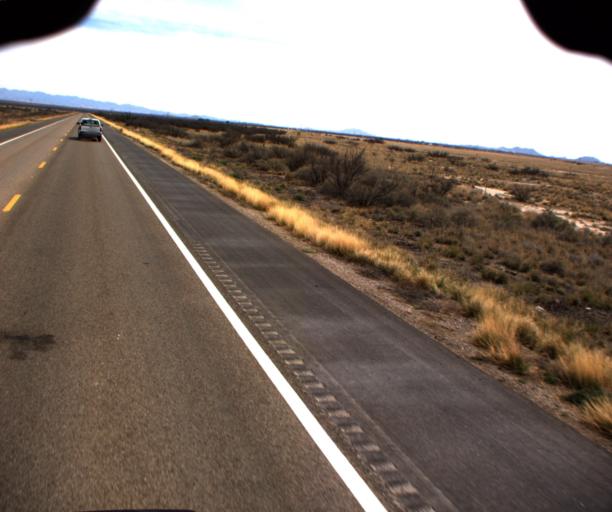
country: US
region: Arizona
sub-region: Cochise County
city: Willcox
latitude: 32.2035
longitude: -109.7696
